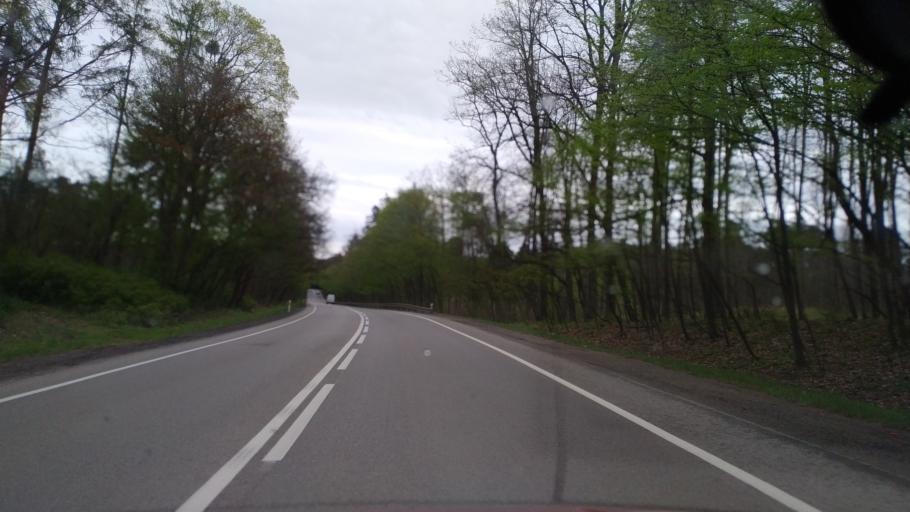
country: PL
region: Pomeranian Voivodeship
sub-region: Powiat starogardzki
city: Starogard Gdanski
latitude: 53.9870
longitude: 18.5793
